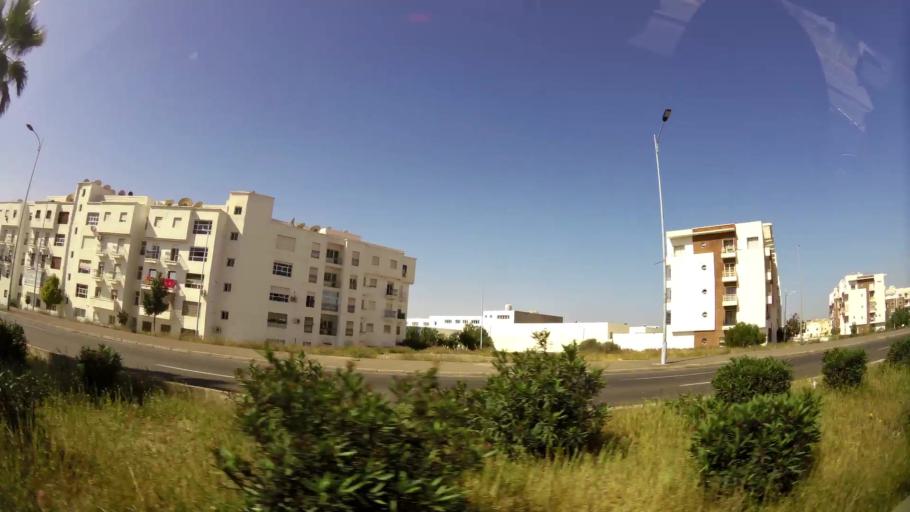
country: MA
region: Oued ed Dahab-Lagouira
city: Dakhla
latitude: 30.4155
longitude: -9.5473
